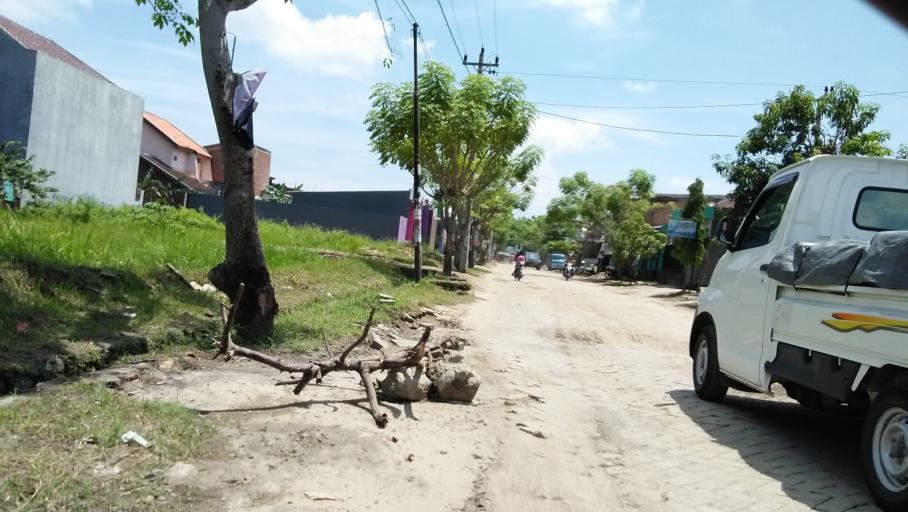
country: ID
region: Central Java
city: Mranggen
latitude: -7.0605
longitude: 110.4683
